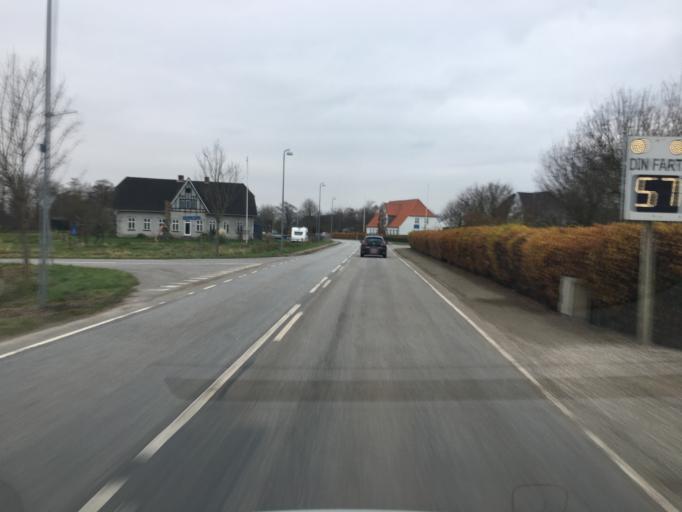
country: DK
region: South Denmark
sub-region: Aabenraa Kommune
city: Tinglev
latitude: 54.9962
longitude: 9.2056
